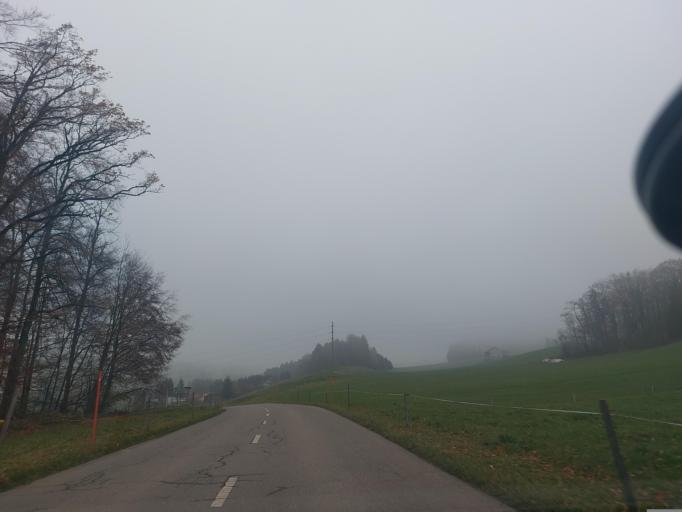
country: CH
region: Fribourg
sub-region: Veveyse District
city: Chatel-Saint-Denis
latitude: 46.5727
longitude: 6.8836
